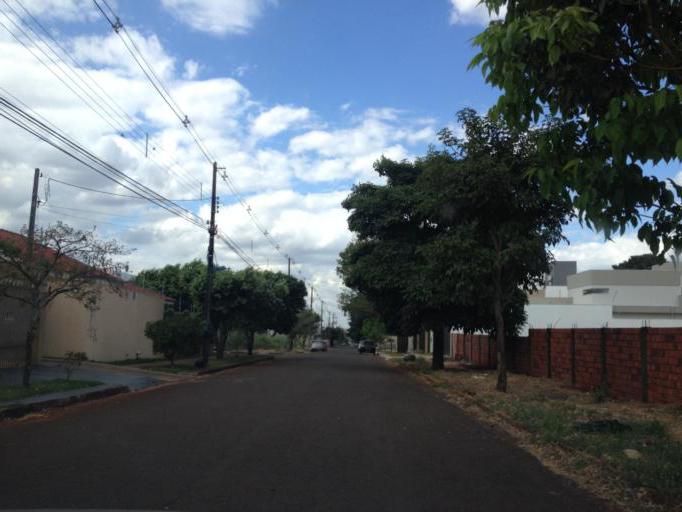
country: BR
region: Parana
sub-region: Maringa
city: Maringa
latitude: -23.4472
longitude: -51.9542
